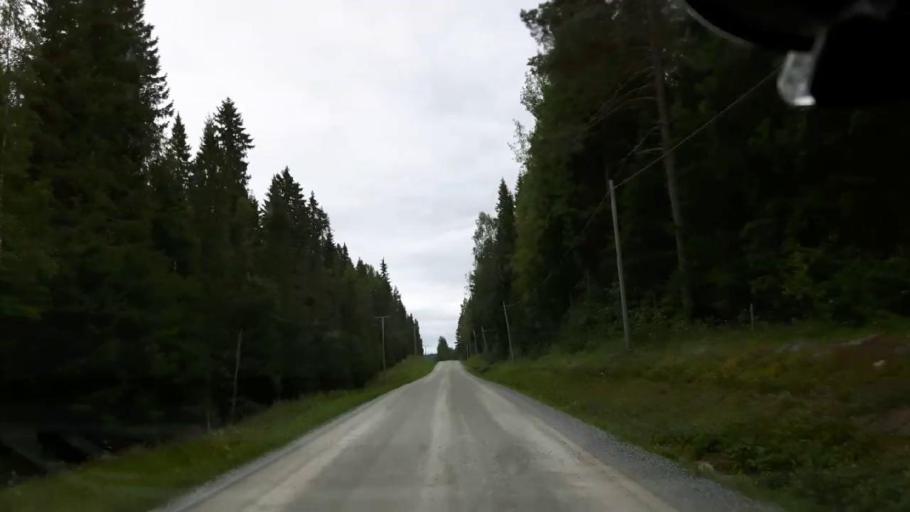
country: SE
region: Jaemtland
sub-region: Braecke Kommun
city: Braecke
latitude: 63.0765
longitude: 15.2922
